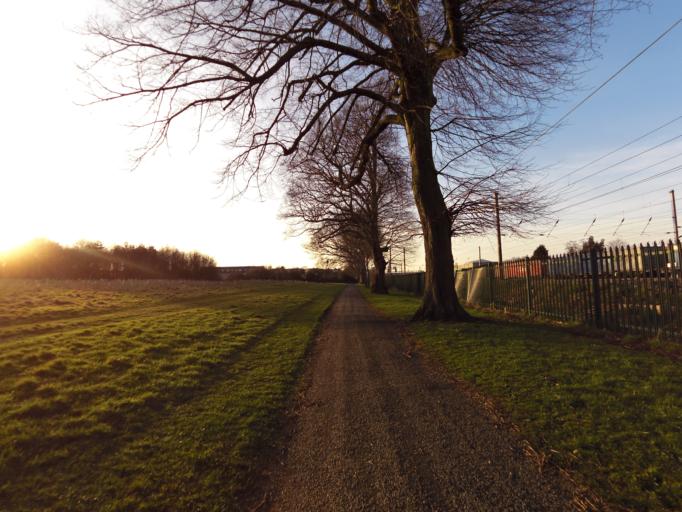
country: GB
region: England
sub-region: Suffolk
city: Ipswich
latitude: 52.0533
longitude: 1.1337
